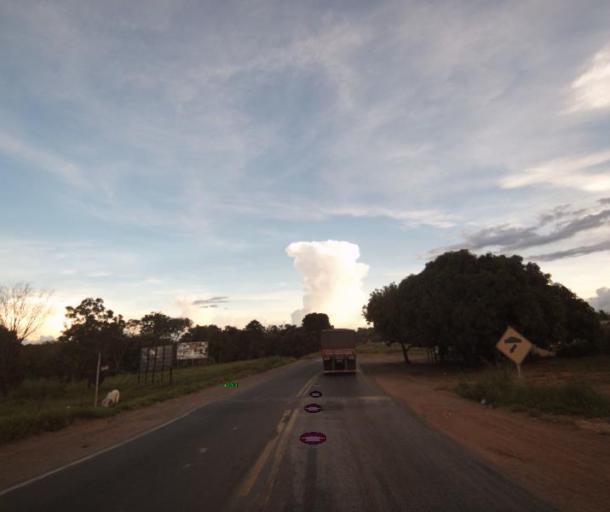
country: BR
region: Goias
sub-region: Uruacu
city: Uruacu
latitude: -14.3171
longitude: -49.1506
